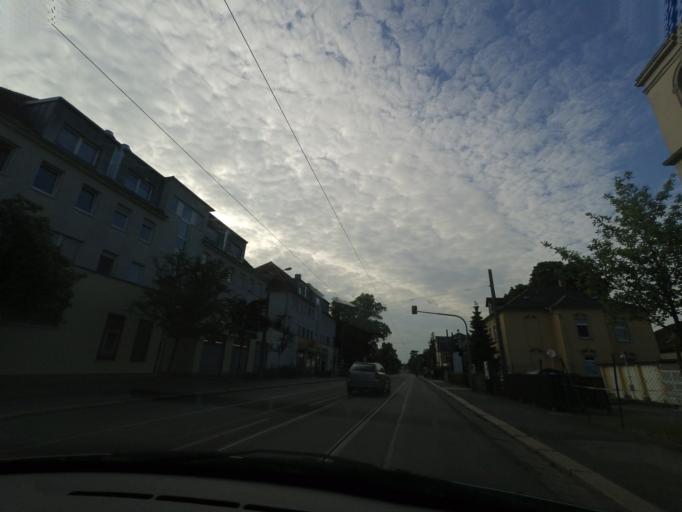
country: DE
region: Saxony
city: Heidenau
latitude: 51.0273
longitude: 13.8353
